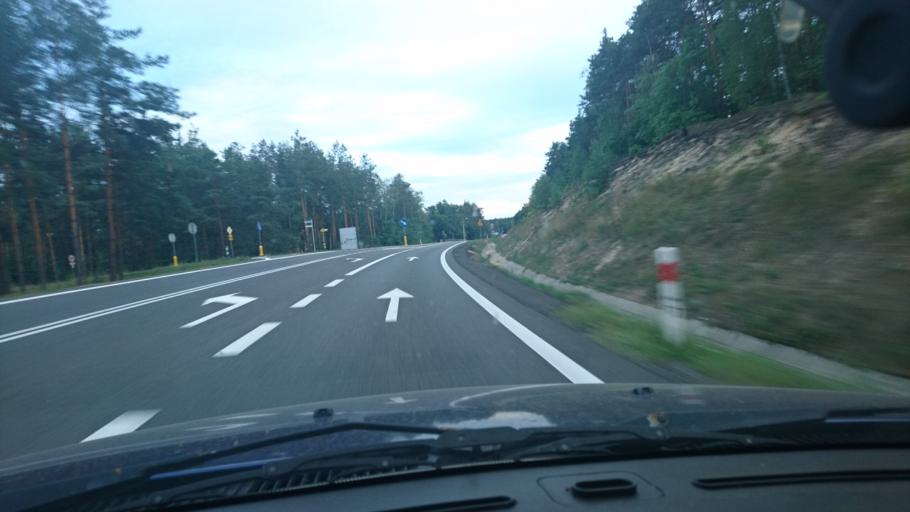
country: PL
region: Silesian Voivodeship
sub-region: Powiat tarnogorski
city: Tworog
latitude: 50.5976
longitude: 18.7028
